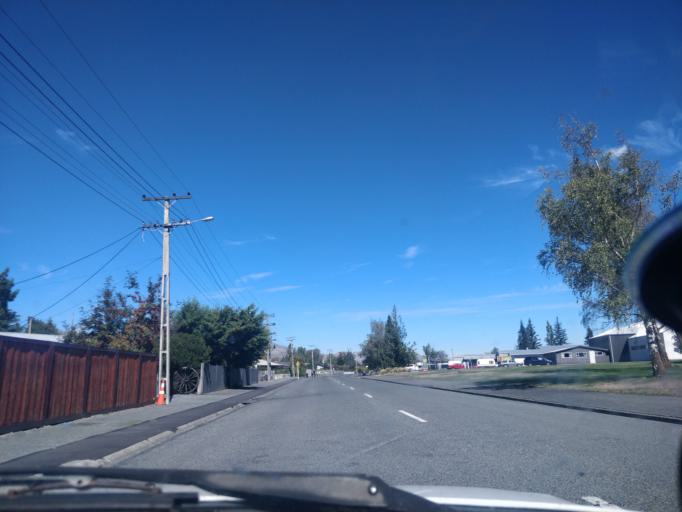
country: NZ
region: Canterbury
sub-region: Timaru District
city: Pleasant Point
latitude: -44.2551
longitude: 170.1014
